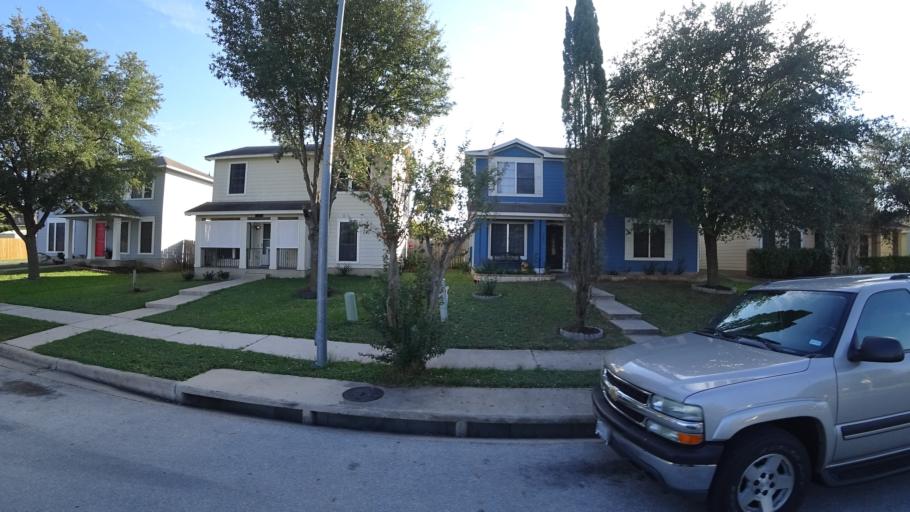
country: US
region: Texas
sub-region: Travis County
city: Wells Branch
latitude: 30.4183
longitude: -97.6562
